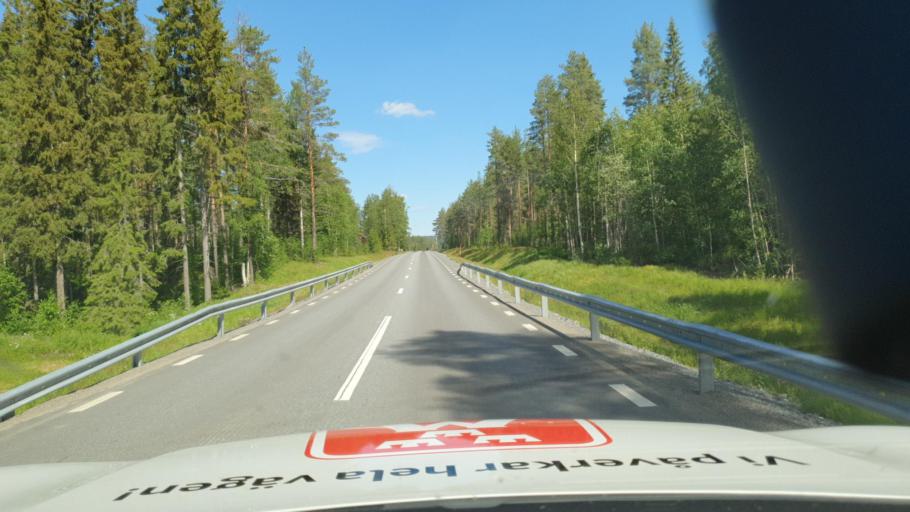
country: SE
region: Vaesterbotten
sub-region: Skelleftea Kommun
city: Langsele
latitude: 64.7797
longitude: 20.3386
